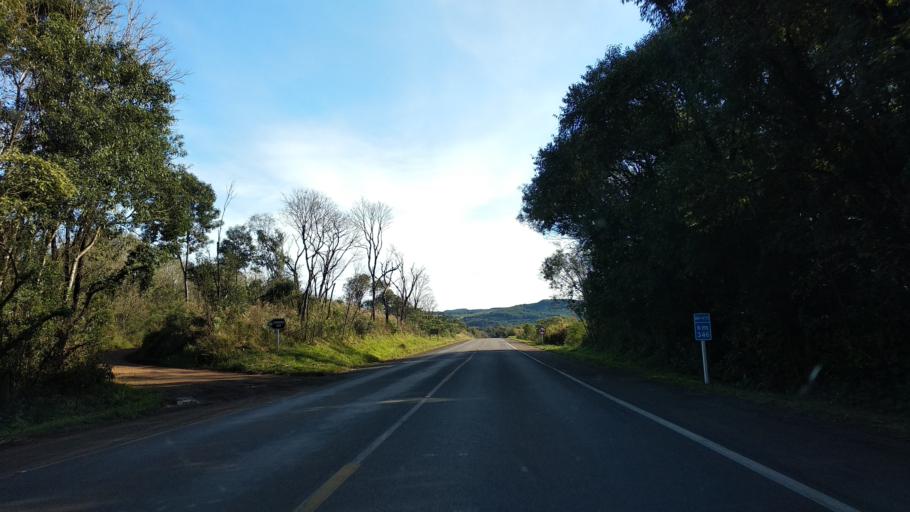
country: BR
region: Santa Catarina
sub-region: Celso Ramos
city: Celso Ramos
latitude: -27.5458
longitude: -51.4285
